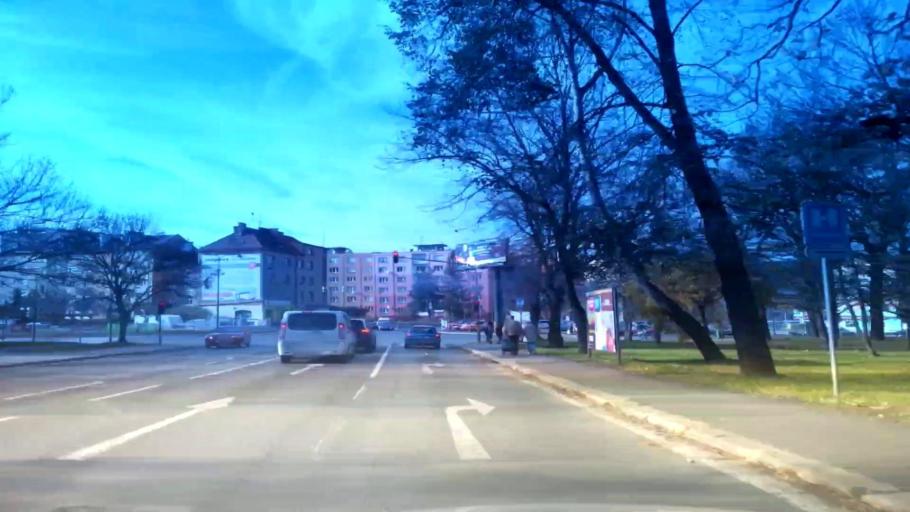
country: CZ
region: Karlovarsky
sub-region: Okres Cheb
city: Cheb
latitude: 50.0776
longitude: 12.3767
